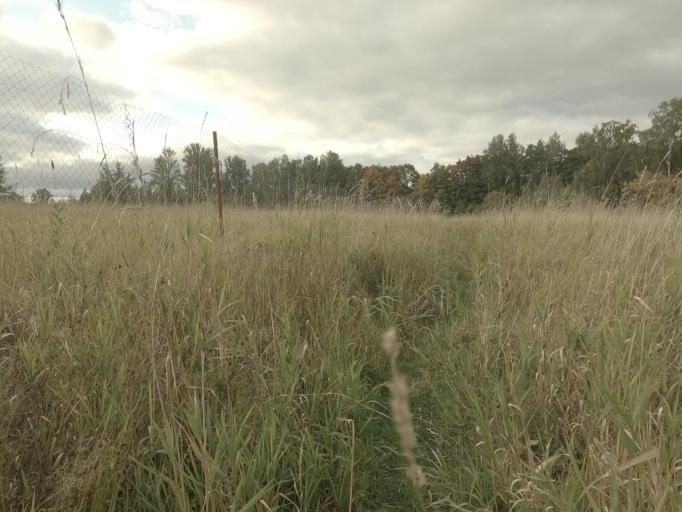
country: RU
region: St.-Petersburg
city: Krasnogvargeisky
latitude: 59.9815
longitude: 30.4928
